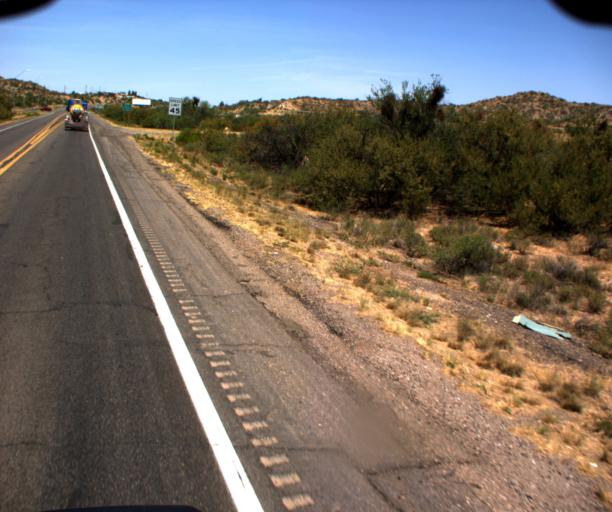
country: US
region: Arizona
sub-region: Gila County
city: Globe
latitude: 33.3727
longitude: -110.7357
